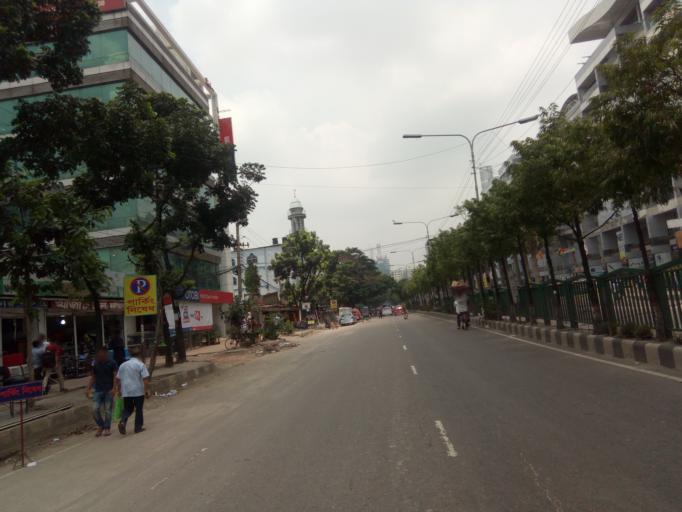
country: BD
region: Dhaka
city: Azimpur
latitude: 23.7502
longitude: 90.3916
